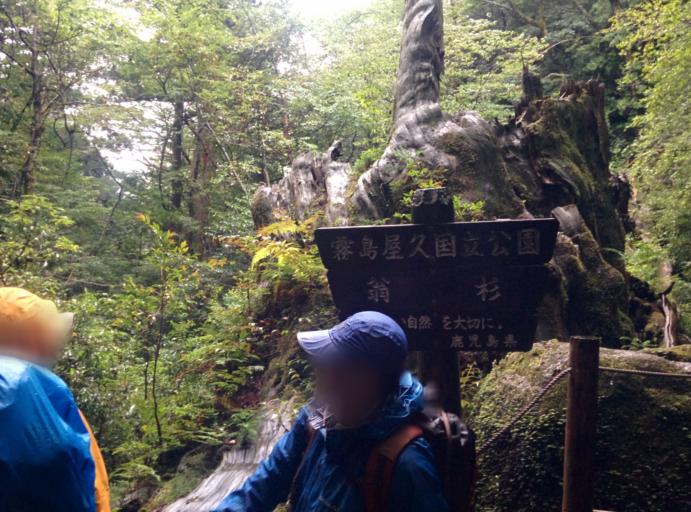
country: JP
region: Kagoshima
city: Nishinoomote
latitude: 30.3553
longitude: 130.5413
